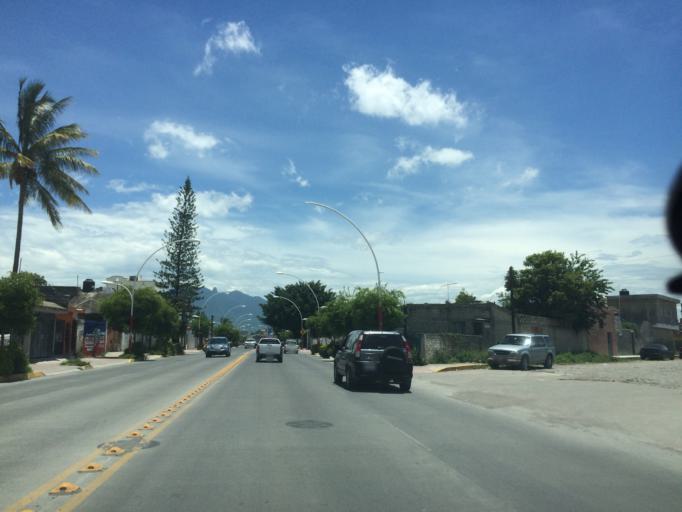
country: MX
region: Nayarit
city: Tepic
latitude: 21.4877
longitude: -104.8703
